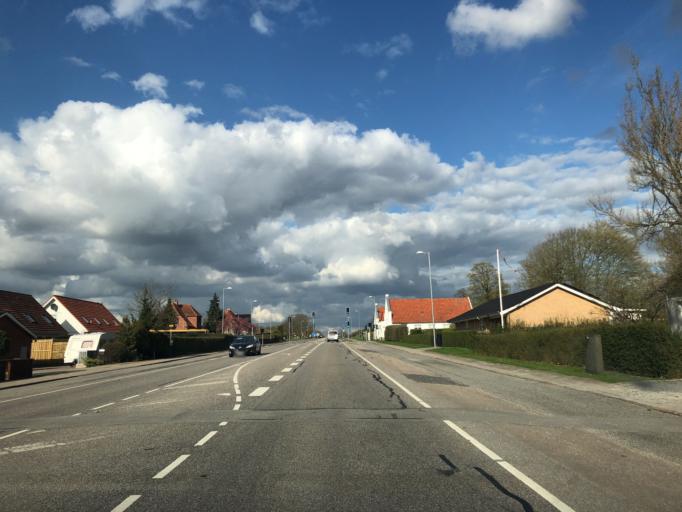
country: DK
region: Zealand
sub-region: Ringsted Kommune
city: Ringsted
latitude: 55.4661
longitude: 11.8112
